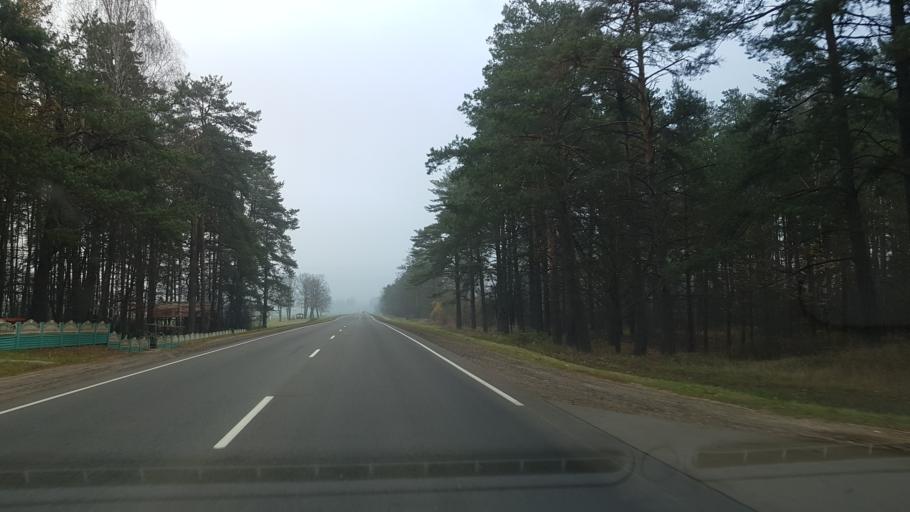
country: BY
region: Mogilev
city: Babruysk
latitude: 53.1669
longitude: 29.3313
